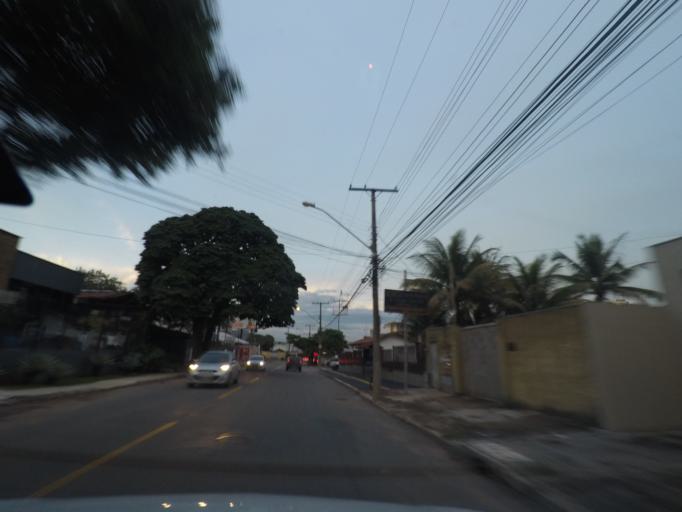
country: BR
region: Goias
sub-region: Goiania
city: Goiania
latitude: -16.7001
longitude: -49.2500
